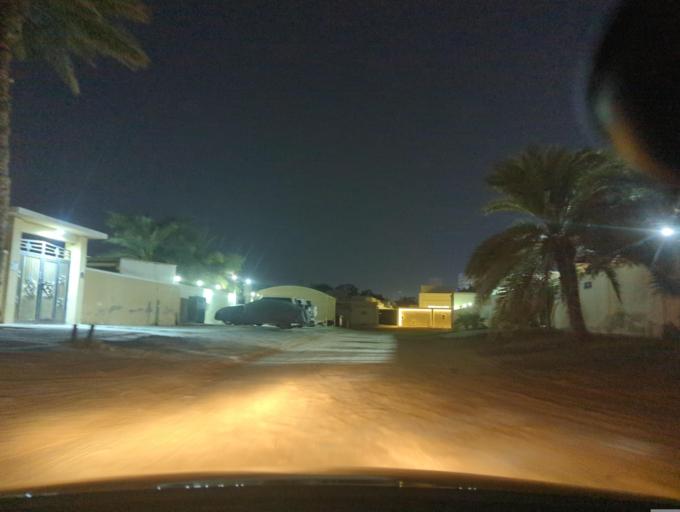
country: AE
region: Ajman
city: Ajman
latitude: 25.3803
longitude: 55.4454
